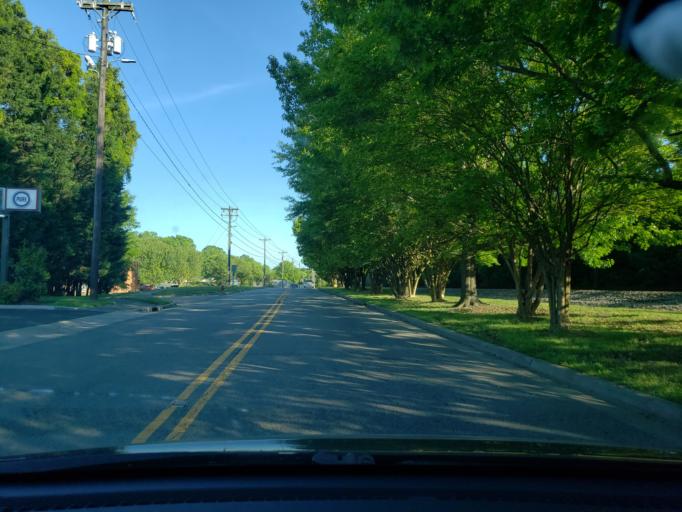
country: US
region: North Carolina
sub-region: Durham County
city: Durham
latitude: 36.0145
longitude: -78.9351
